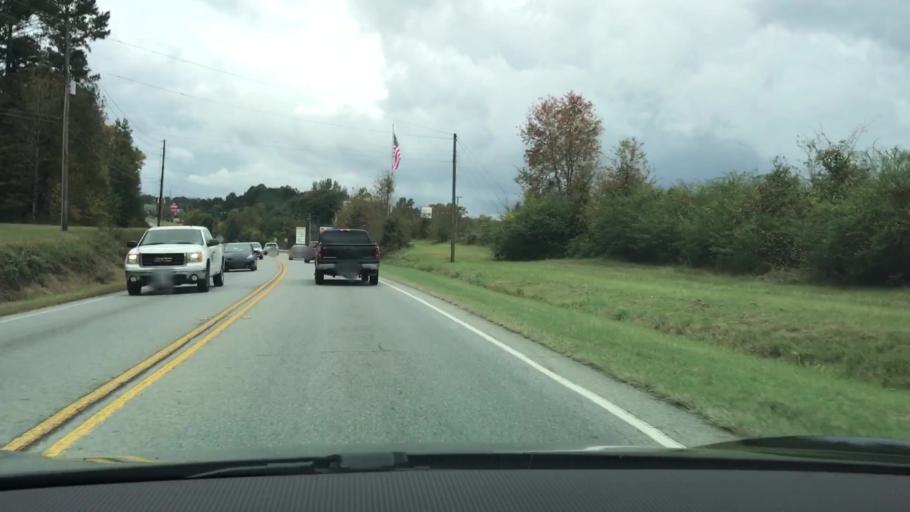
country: US
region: Georgia
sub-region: Greene County
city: Greensboro
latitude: 33.5530
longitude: -83.1989
